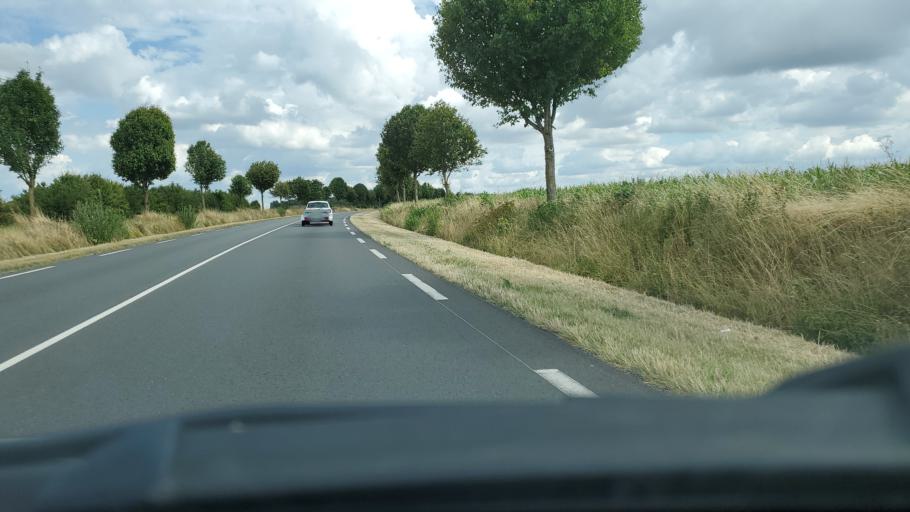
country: FR
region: Ile-de-France
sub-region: Departement de Seine-et-Marne
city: Nanteuil-les-Meaux
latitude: 48.9141
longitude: 2.9125
